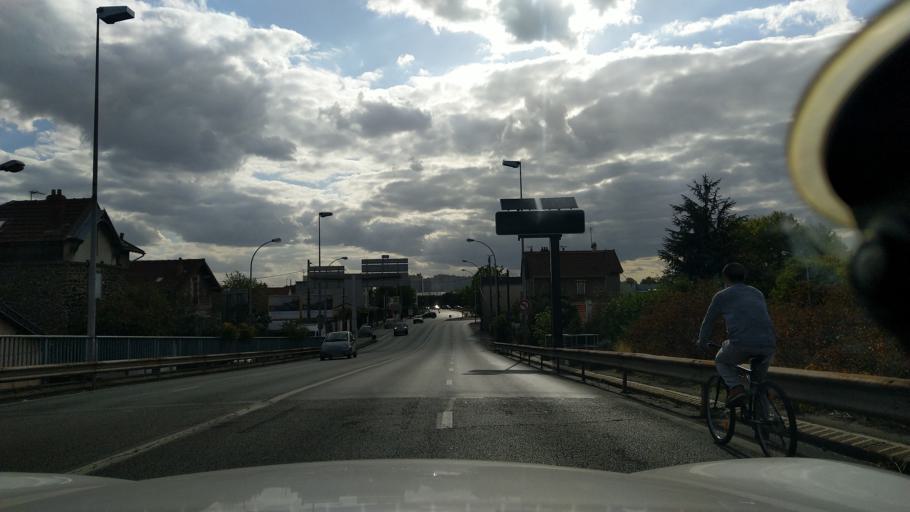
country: FR
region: Ile-de-France
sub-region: Departement de Seine-Saint-Denis
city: Aulnay-sous-Bois
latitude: 48.9317
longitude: 2.4855
